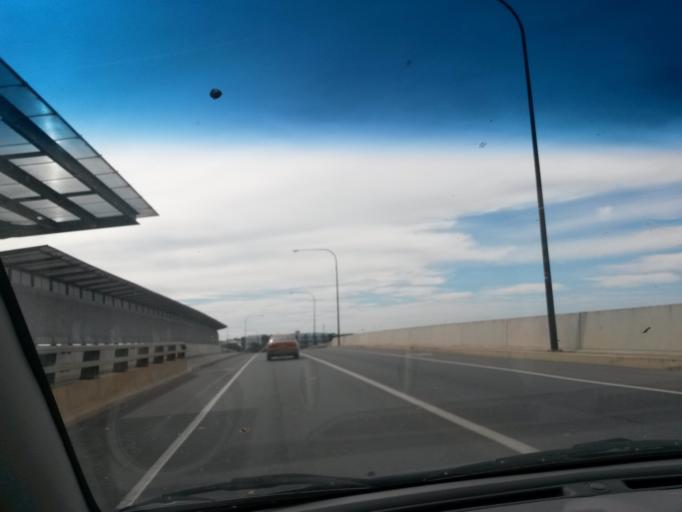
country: AU
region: South Australia
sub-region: Salisbury
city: Ingle Farm
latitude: -34.8036
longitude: 138.6127
